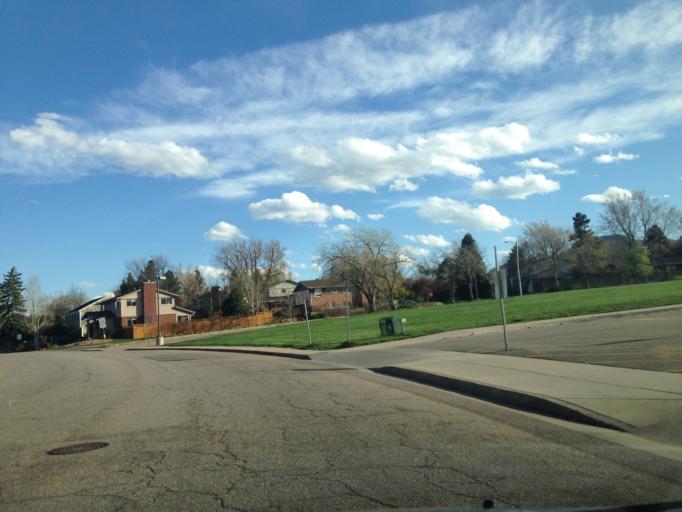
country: US
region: Colorado
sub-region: Boulder County
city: Boulder
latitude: 39.9810
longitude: -105.2513
